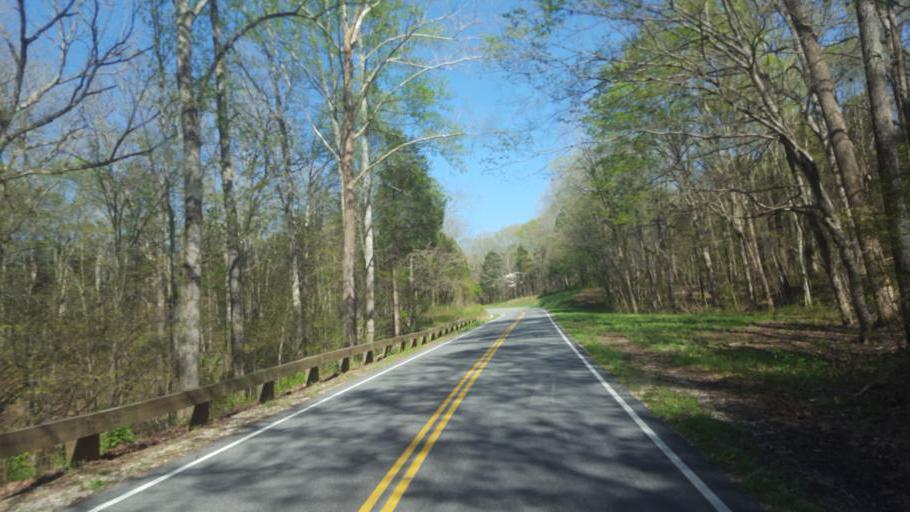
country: US
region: Kentucky
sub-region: Edmonson County
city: Brownsville
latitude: 37.1583
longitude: -86.1550
